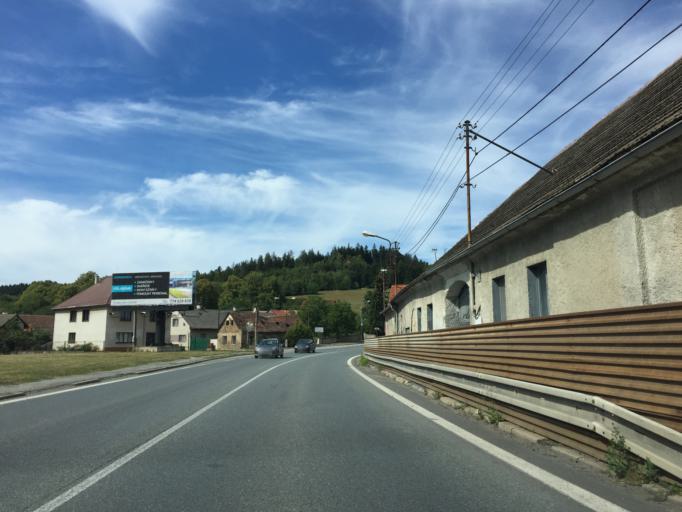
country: CZ
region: Central Bohemia
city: Votice
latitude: 49.5706
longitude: 14.6587
